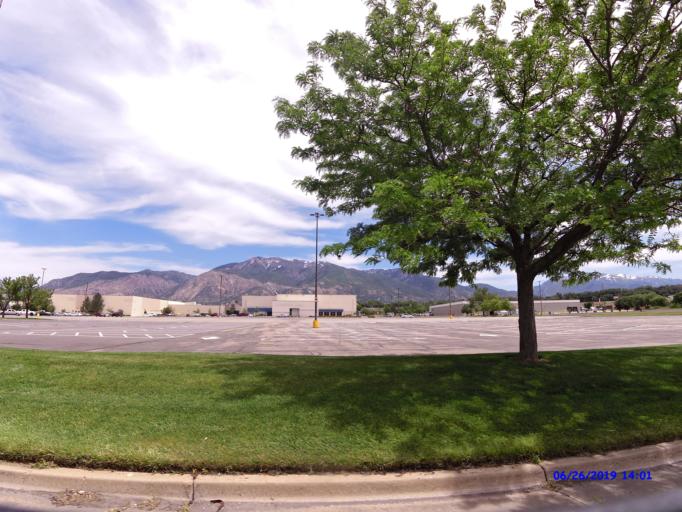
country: US
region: Utah
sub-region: Weber County
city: South Ogden
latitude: 41.1935
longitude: -111.9858
